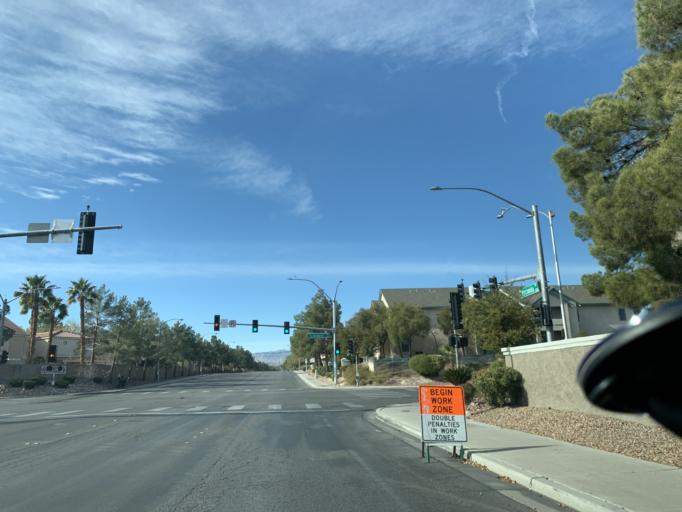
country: US
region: Nevada
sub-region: Clark County
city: Spring Valley
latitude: 36.0932
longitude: -115.2162
